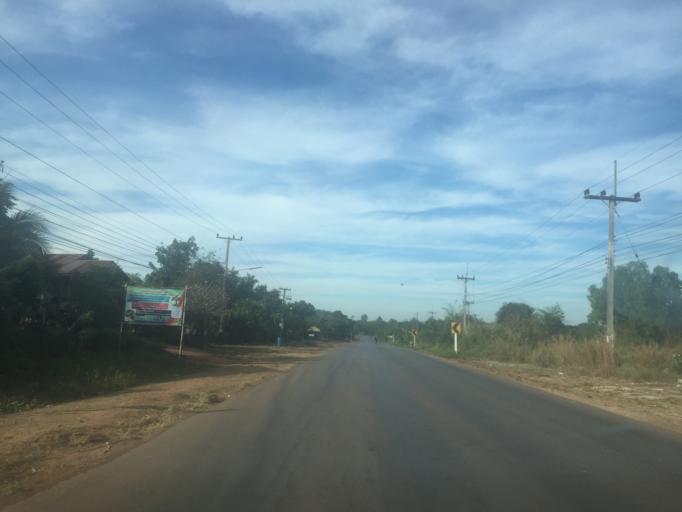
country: TH
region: Changwat Udon Thani
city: Si That
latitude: 16.9898
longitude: 103.1691
